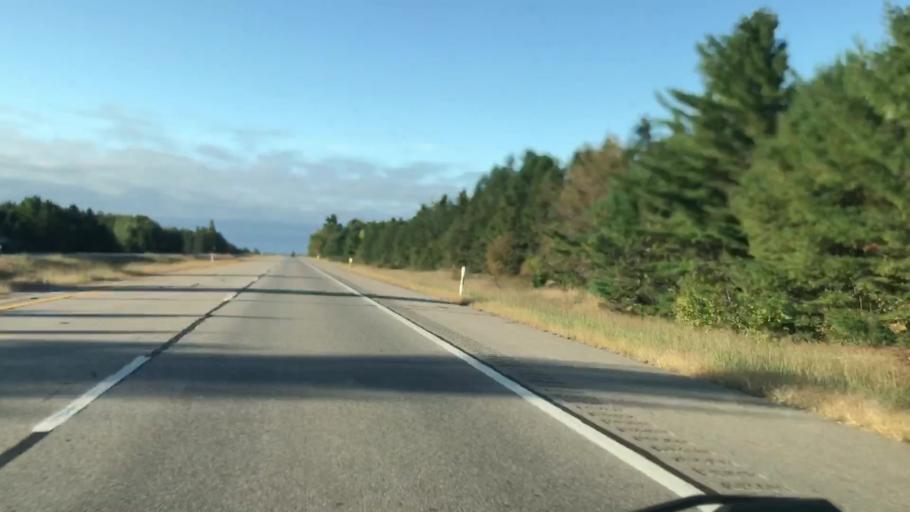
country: US
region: Michigan
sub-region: Chippewa County
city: Sault Ste. Marie
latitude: 46.4305
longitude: -84.3911
